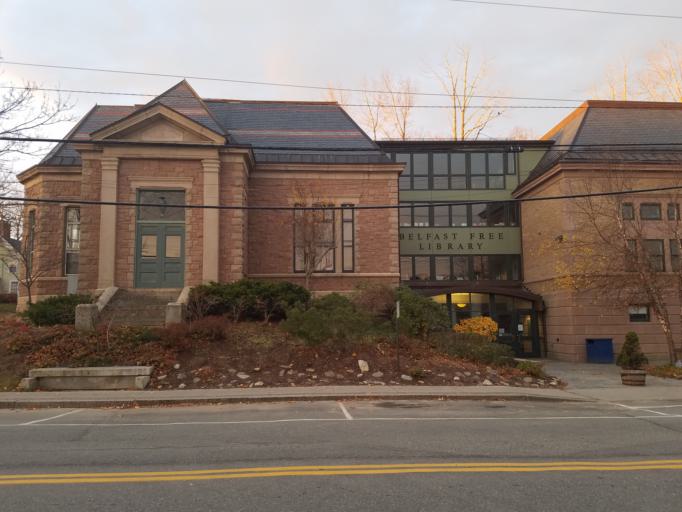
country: US
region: Maine
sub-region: Waldo County
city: Belfast
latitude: 44.4252
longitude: -69.0046
